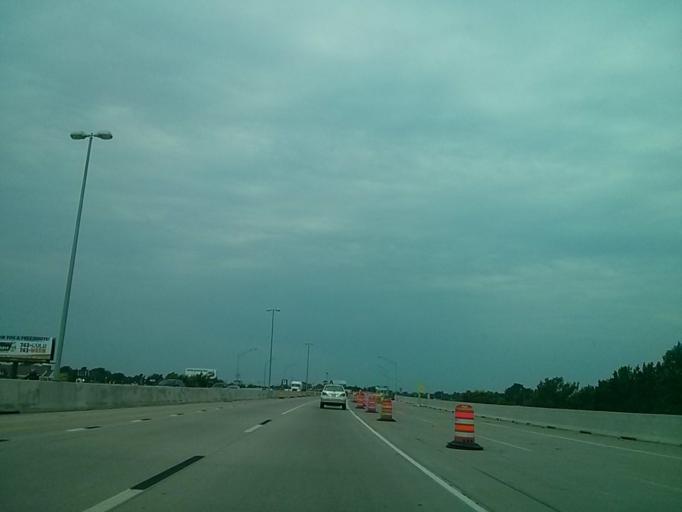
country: US
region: Oklahoma
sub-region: Tulsa County
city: Tulsa
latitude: 36.1621
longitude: -95.8920
